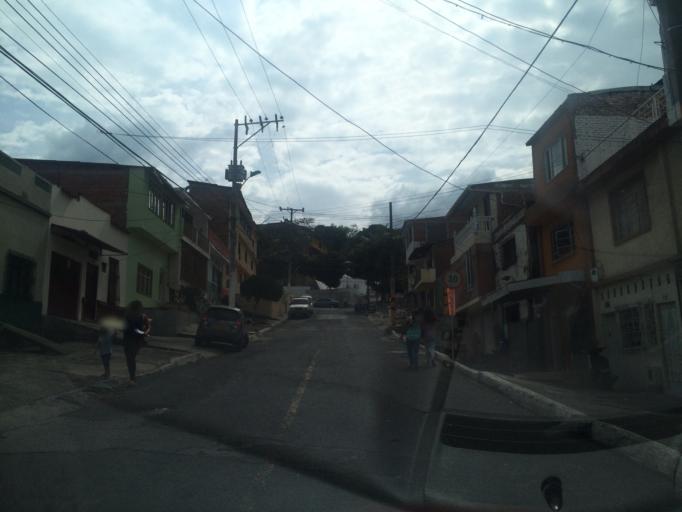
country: CO
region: Valle del Cauca
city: Cali
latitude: 3.4447
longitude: -76.5423
